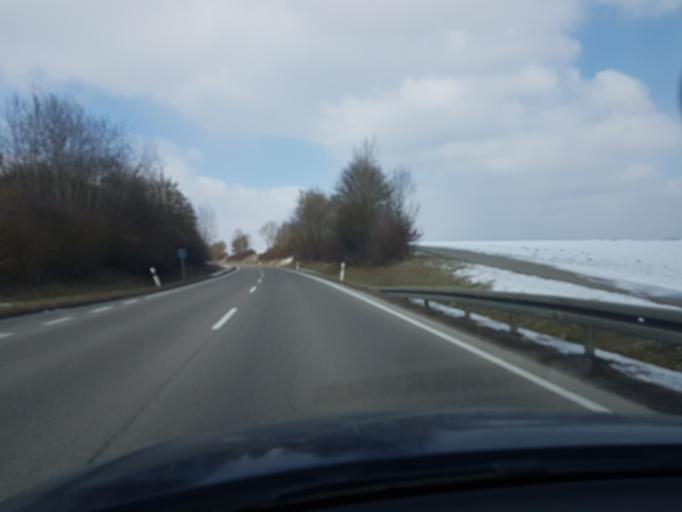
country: DE
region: Baden-Wuerttemberg
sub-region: Regierungsbezirk Stuttgart
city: Bondorf
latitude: 48.5301
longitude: 8.8444
